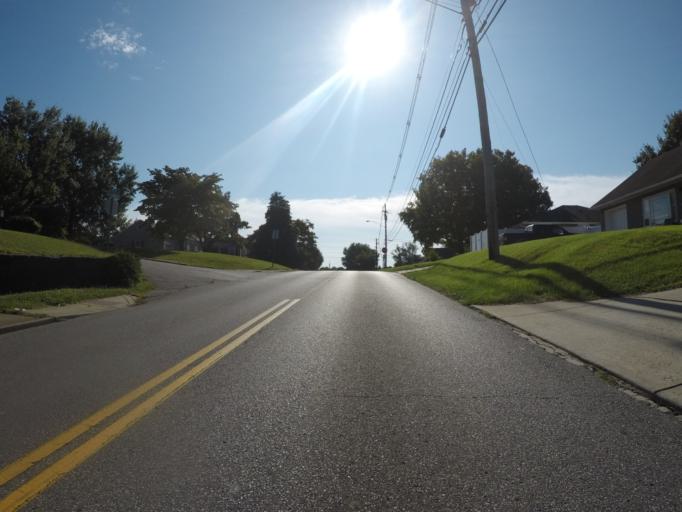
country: US
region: Kentucky
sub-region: Boyd County
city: Ashland
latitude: 38.4511
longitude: -82.6314
